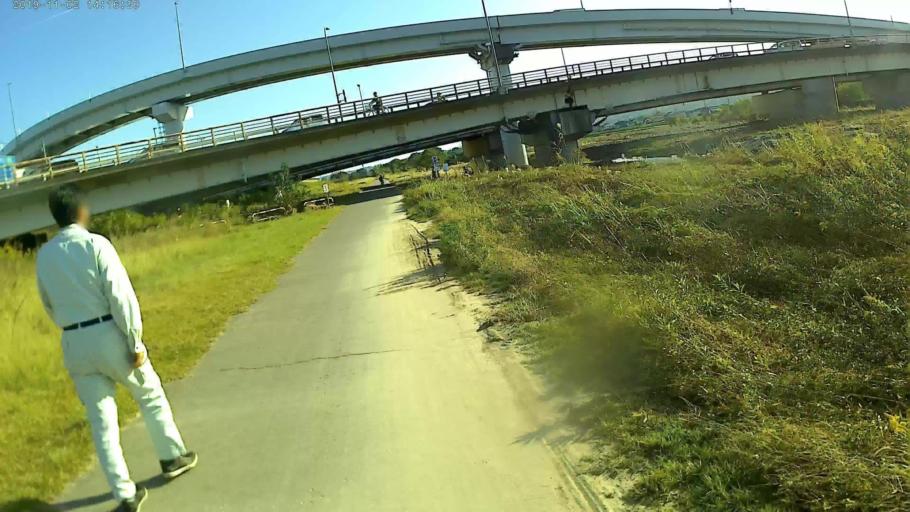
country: JP
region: Gunma
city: Takasaki
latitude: 36.3338
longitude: 138.9905
